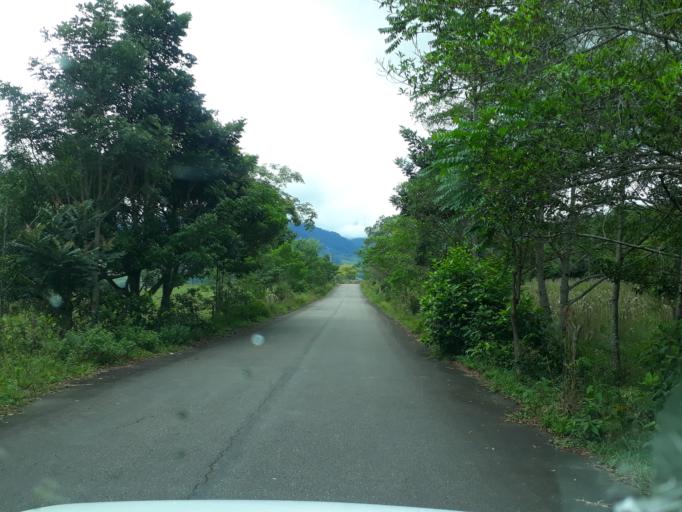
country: CO
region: Cundinamarca
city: Medina
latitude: 4.5797
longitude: -73.3604
